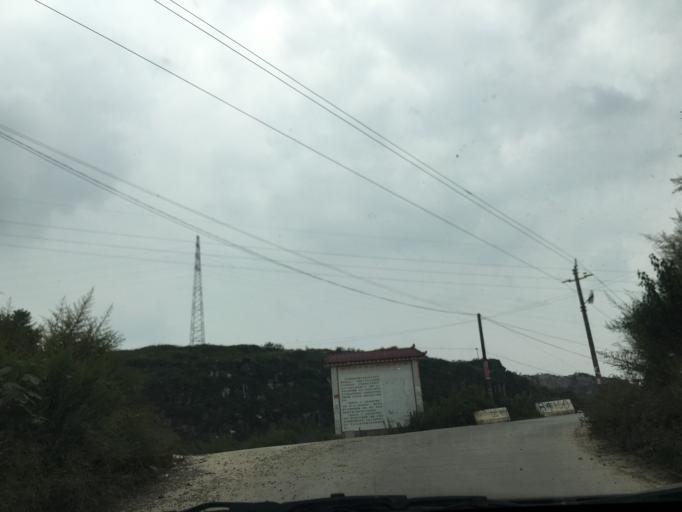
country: CN
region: Guangxi Zhuangzu Zizhiqu
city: Xinzhou
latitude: 25.5295
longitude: 105.6324
